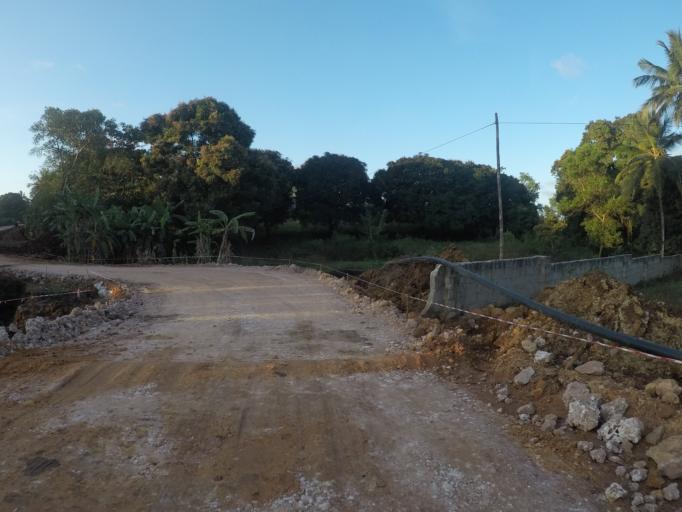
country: TZ
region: Zanzibar North
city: Gamba
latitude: -5.9193
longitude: 39.2998
